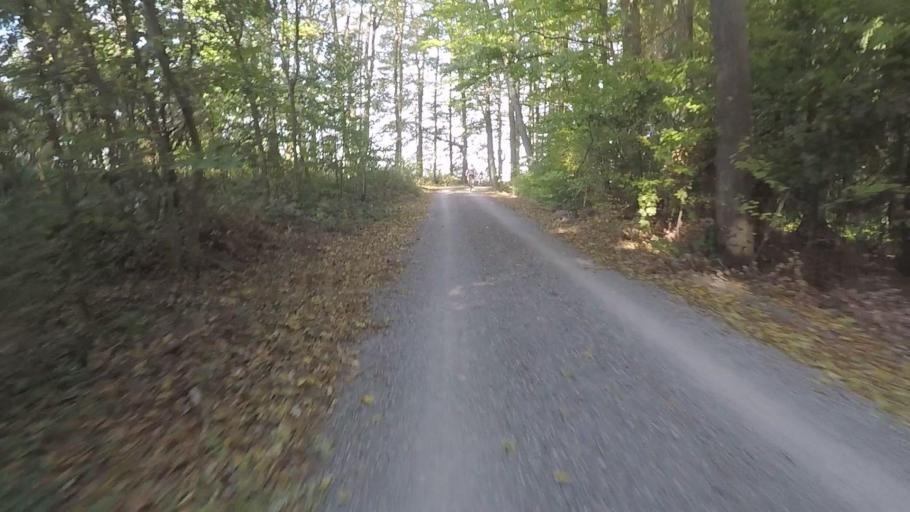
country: DE
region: Baden-Wuerttemberg
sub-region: Regierungsbezirk Stuttgart
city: Wustenrot
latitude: 49.0631
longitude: 9.4810
